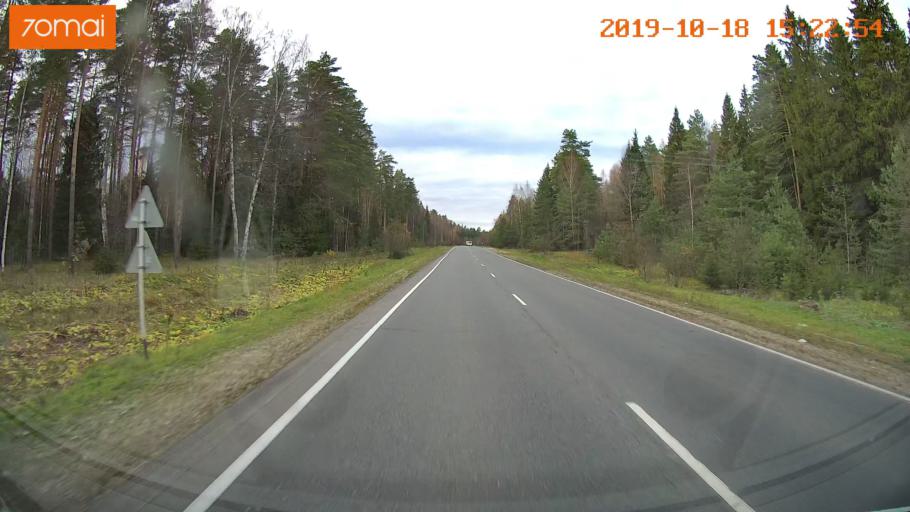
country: RU
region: Vladimir
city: Anopino
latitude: 55.7130
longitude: 40.7274
